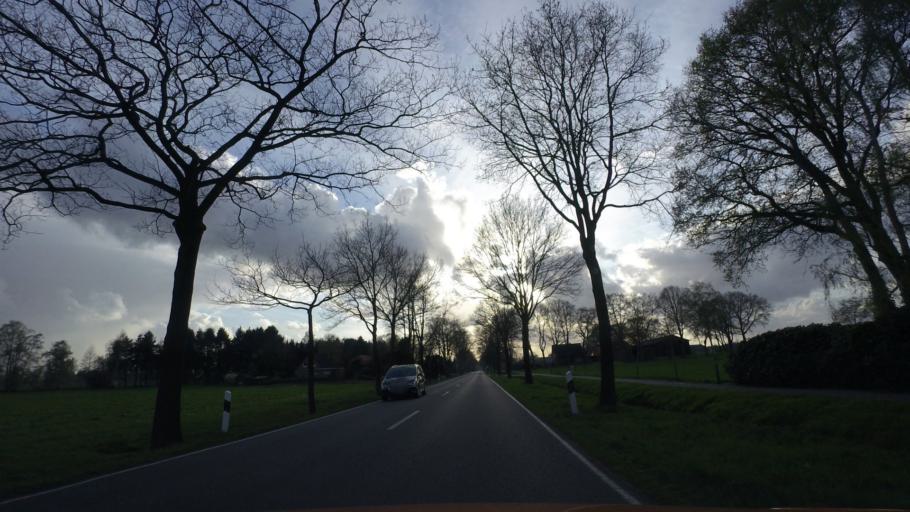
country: DE
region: Lower Saxony
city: Edewecht
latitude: 53.1237
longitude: 8.0694
